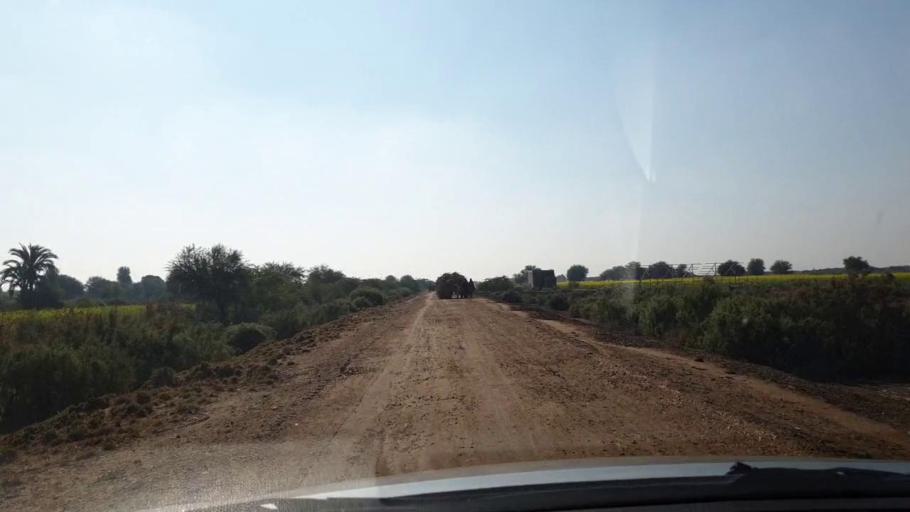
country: PK
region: Sindh
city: Jhol
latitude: 25.8702
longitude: 68.8953
